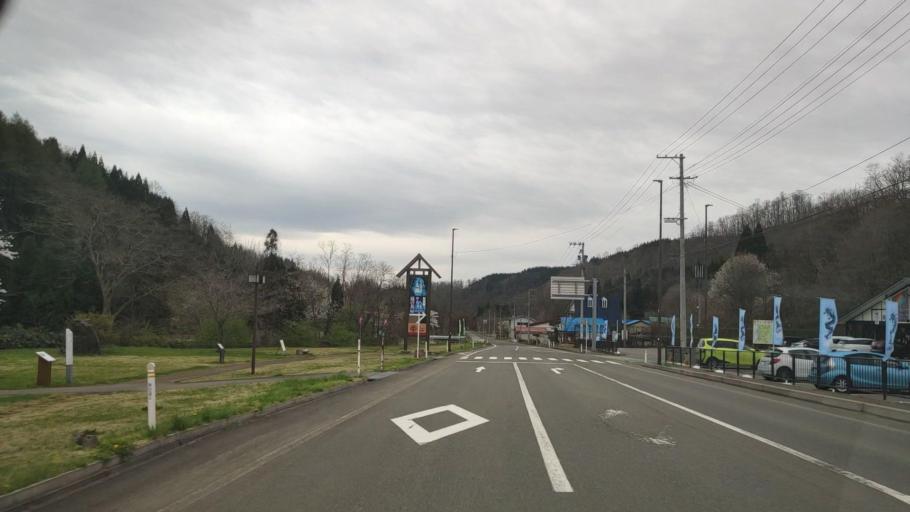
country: JP
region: Akita
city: Hanawa
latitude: 40.3569
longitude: 140.7830
